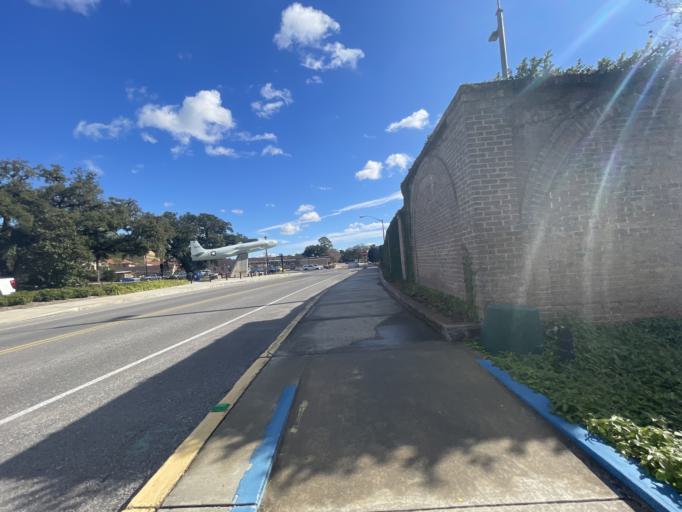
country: US
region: Louisiana
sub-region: East Baton Rouge Parish
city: Baton Rouge
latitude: 30.4100
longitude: -91.1816
